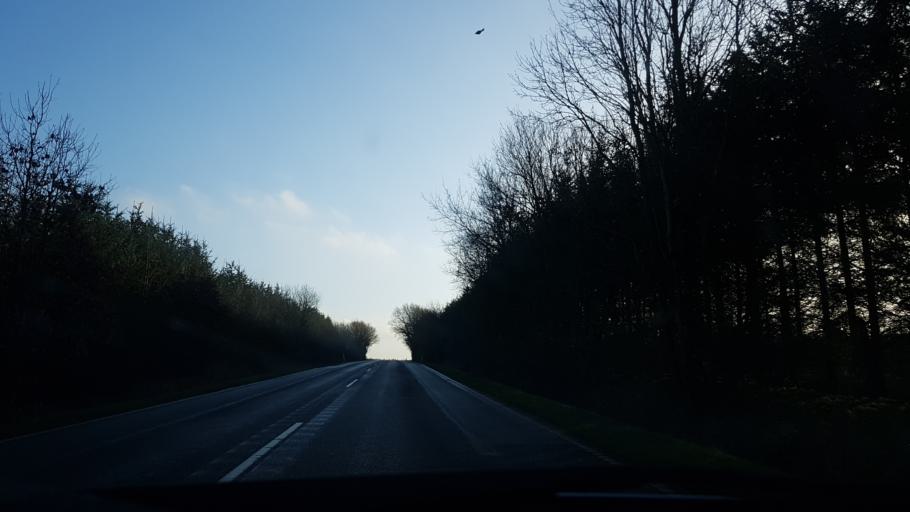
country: DK
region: South Denmark
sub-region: Tonder Kommune
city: Toftlund
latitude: 55.2189
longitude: 9.1811
